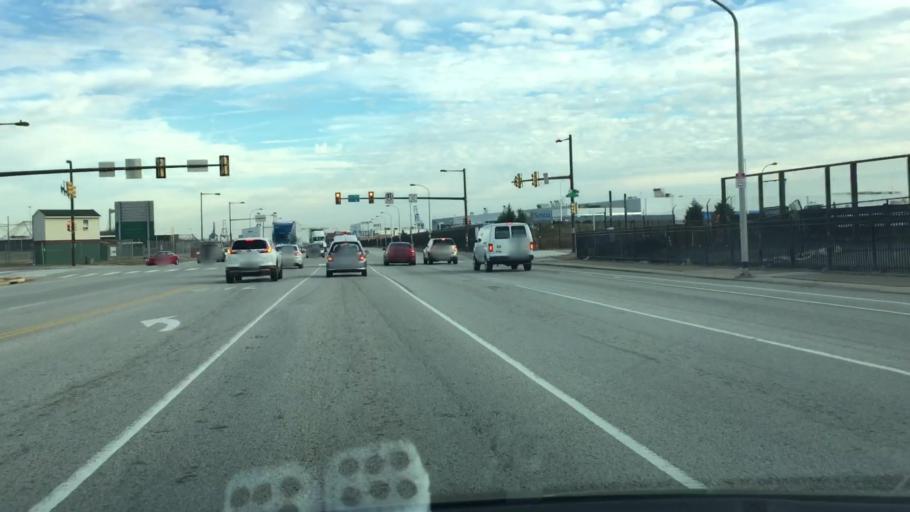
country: US
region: Pennsylvania
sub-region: Philadelphia County
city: Philadelphia
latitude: 39.9096
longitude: -75.1619
